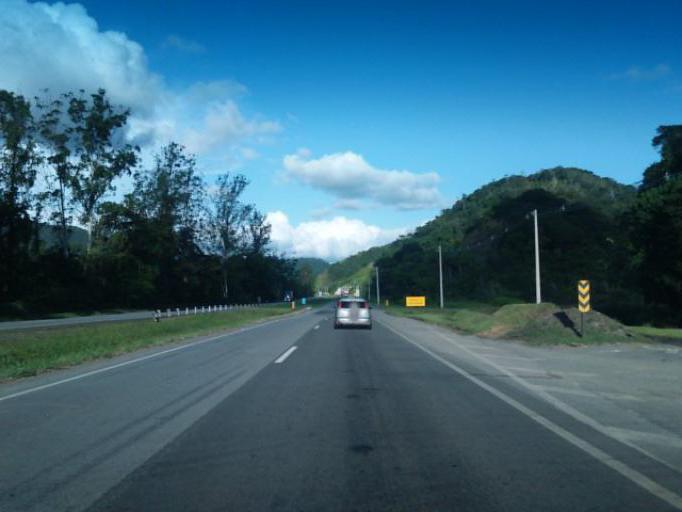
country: BR
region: Sao Paulo
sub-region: Miracatu
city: Miracatu
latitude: -24.1507
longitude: -47.3137
